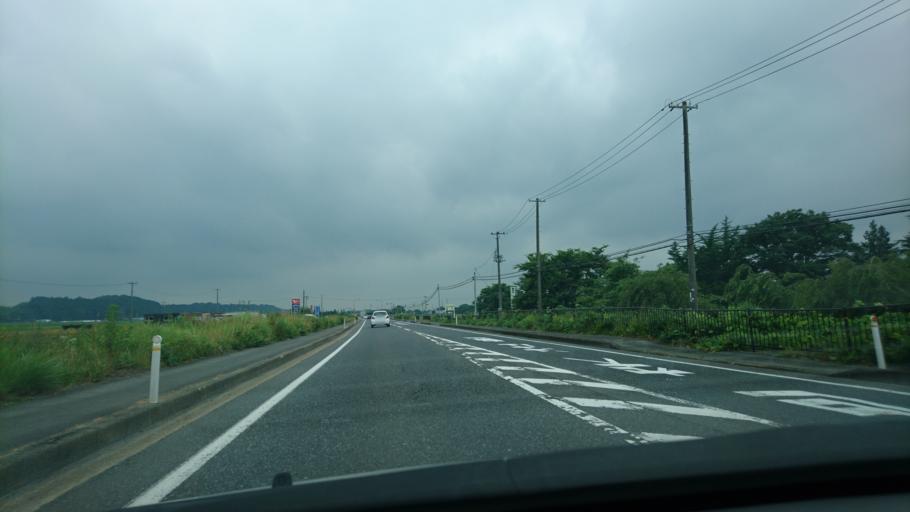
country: JP
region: Miyagi
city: Furukawa
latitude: 38.6659
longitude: 140.8699
